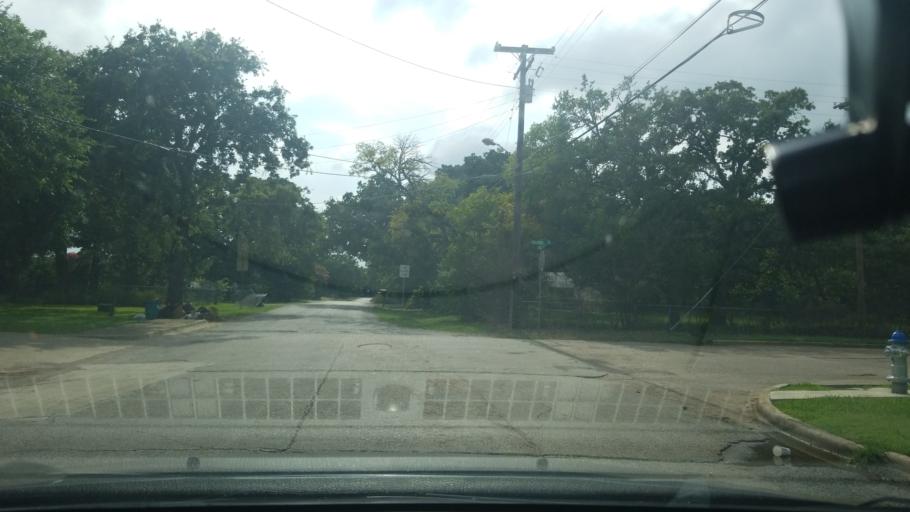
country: US
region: Texas
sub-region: Dallas County
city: Balch Springs
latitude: 32.7576
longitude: -96.6353
